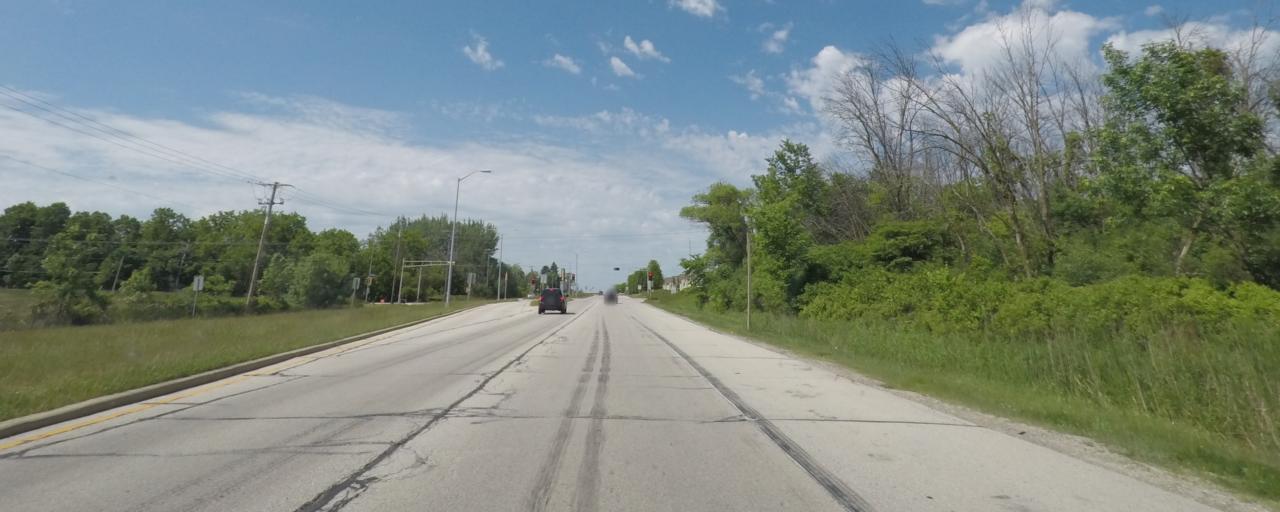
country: US
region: Wisconsin
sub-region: Milwaukee County
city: Greendale
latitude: 42.8861
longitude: -87.9507
